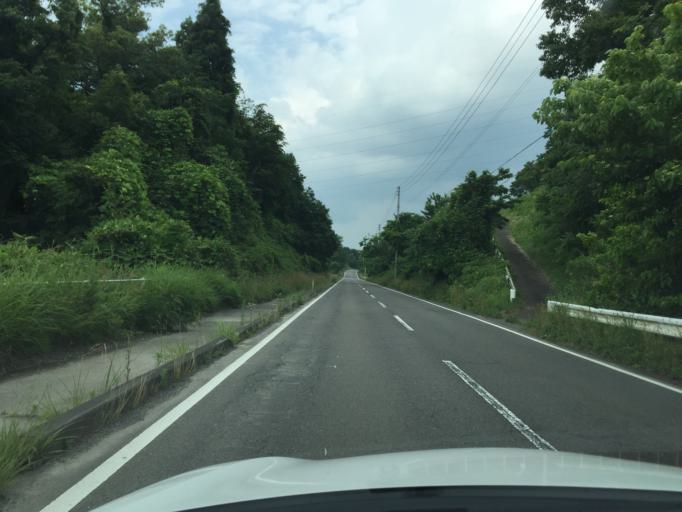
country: JP
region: Fukushima
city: Sukagawa
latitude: 37.2987
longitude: 140.4344
